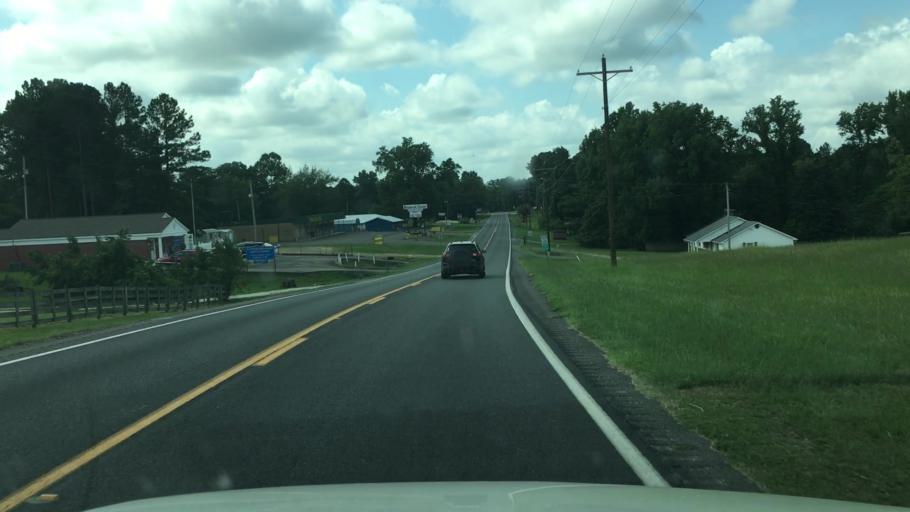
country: US
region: Arkansas
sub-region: Garland County
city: Lake Hamilton
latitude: 34.3250
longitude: -93.1731
